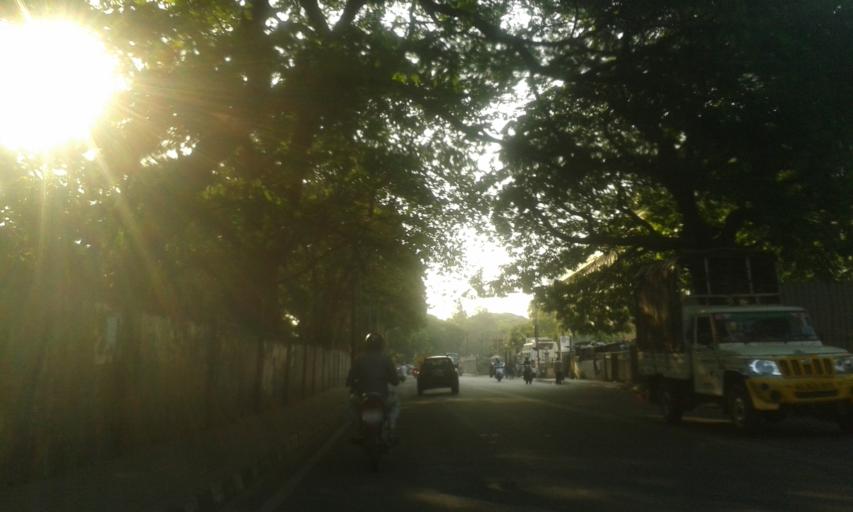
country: IN
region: Karnataka
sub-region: Bangalore Urban
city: Bangalore
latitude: 12.9521
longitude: 77.5888
